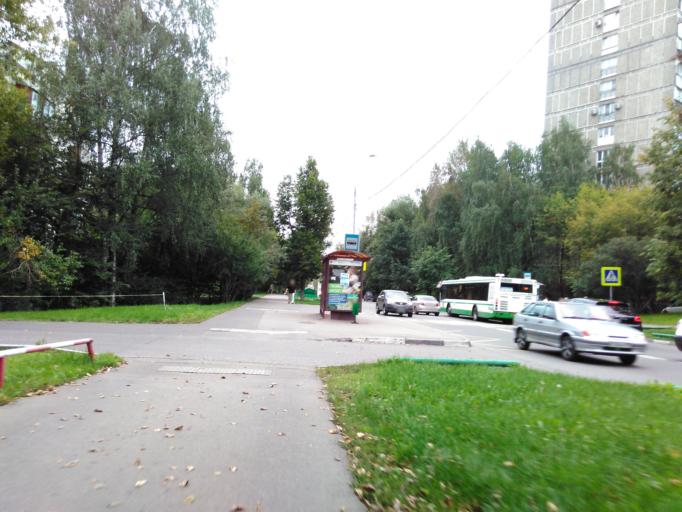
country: RU
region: Moscow
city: Zyuzino
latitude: 55.6620
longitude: 37.5845
